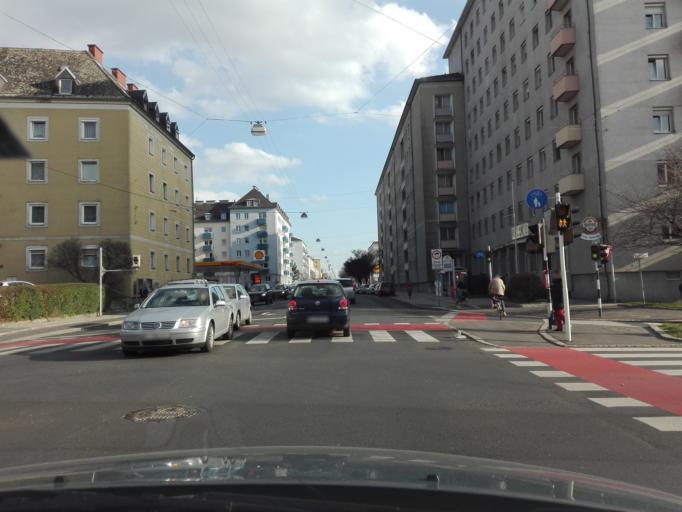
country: AT
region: Upper Austria
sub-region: Linz Stadt
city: Linz
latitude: 48.2967
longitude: 14.3069
